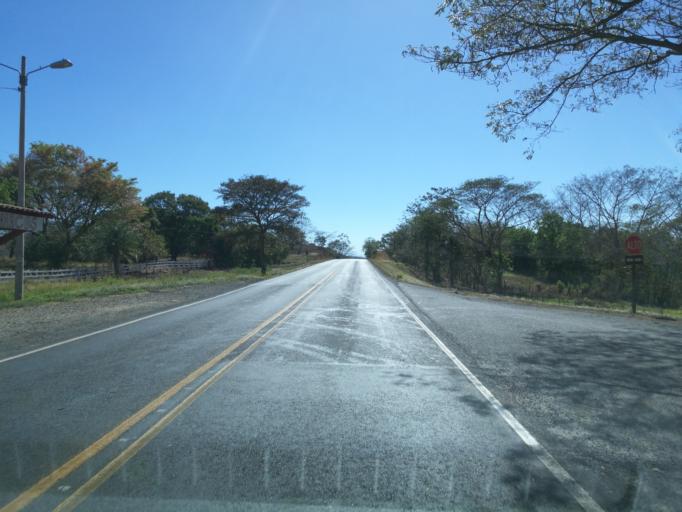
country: CR
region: Puntarenas
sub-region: Canton Central de Puntarenas
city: Puntarenas
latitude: 10.0994
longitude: -84.8671
